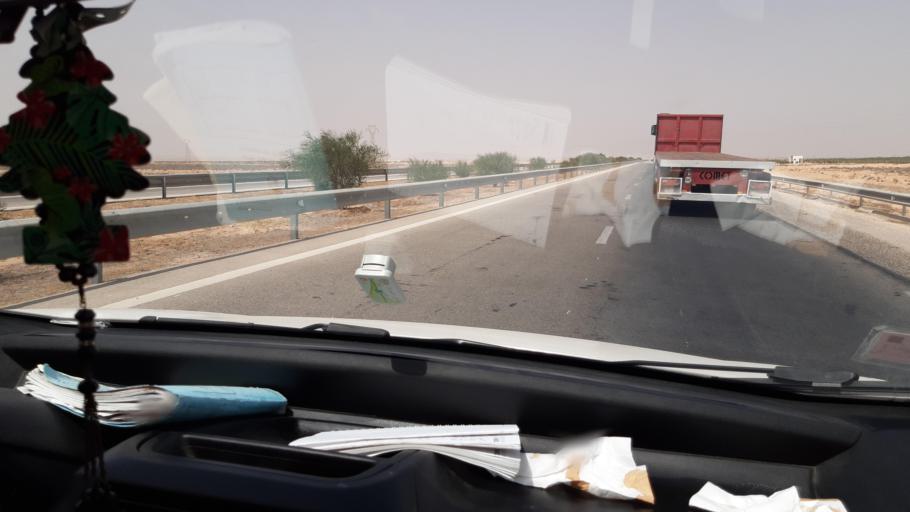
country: TN
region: Qabis
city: Gabes
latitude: 33.9386
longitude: 9.9618
